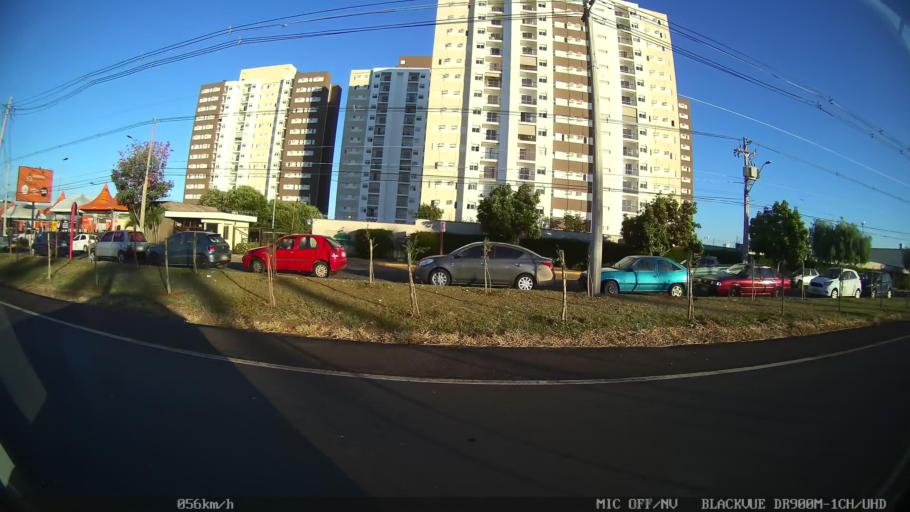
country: BR
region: Sao Paulo
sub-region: Araraquara
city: Araraquara
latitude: -21.7846
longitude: -48.2002
